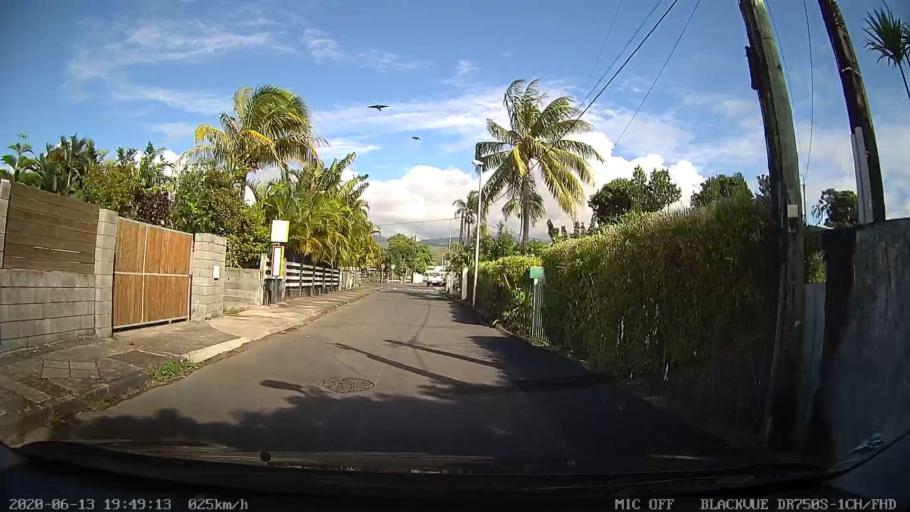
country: RE
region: Reunion
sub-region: Reunion
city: Bras-Panon
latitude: -21.0041
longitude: 55.6894
